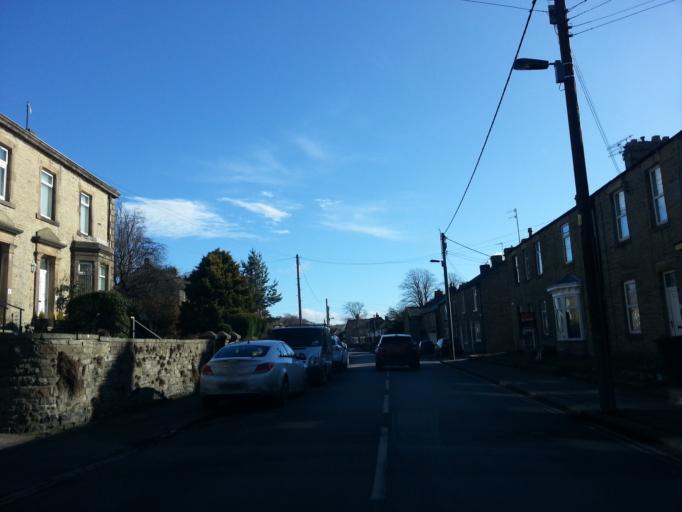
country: GB
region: England
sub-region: County Durham
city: Stanhope
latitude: 54.7452
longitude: -2.0023
